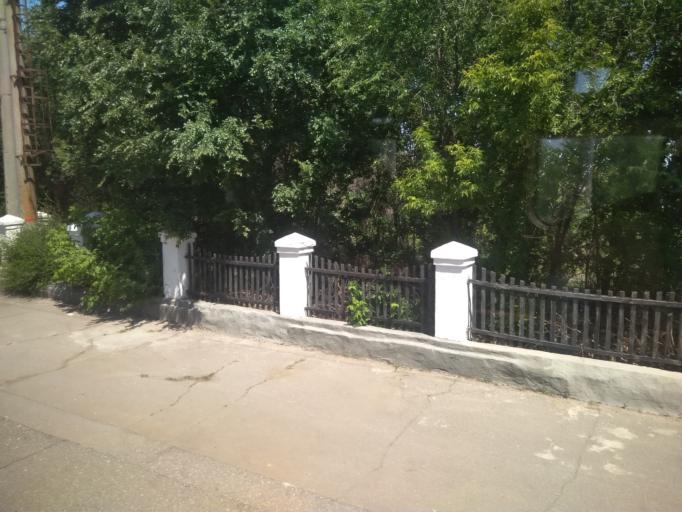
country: RU
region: Volgograd
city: Krasnoslobodsk
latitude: 48.5189
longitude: 44.5130
